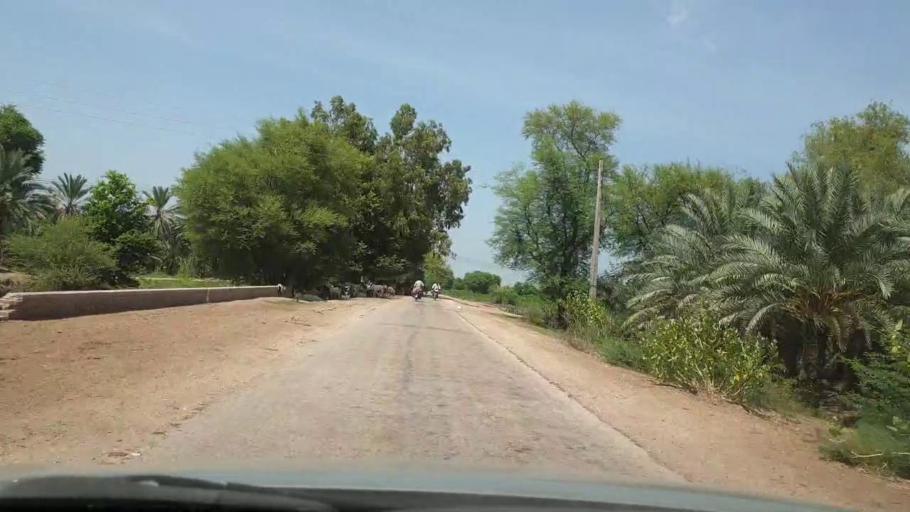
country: PK
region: Sindh
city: Pano Aqil
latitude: 27.7001
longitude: 69.1121
